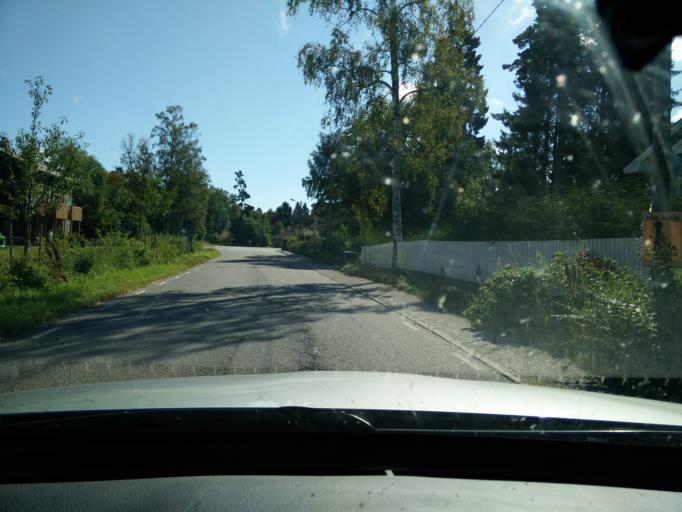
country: SE
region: Stockholm
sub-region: Lidingo
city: Lidingoe
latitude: 59.4653
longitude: 18.1811
